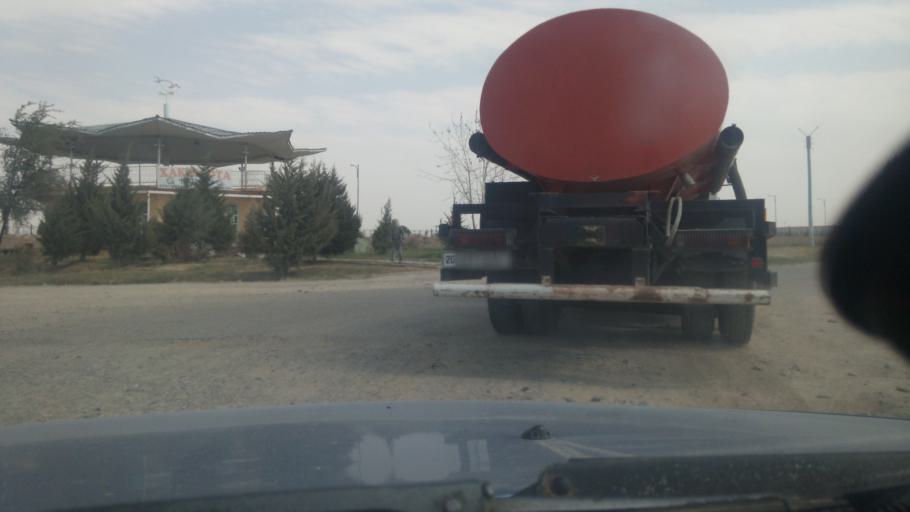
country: UZ
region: Sirdaryo
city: Guliston
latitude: 40.5010
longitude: 68.7827
